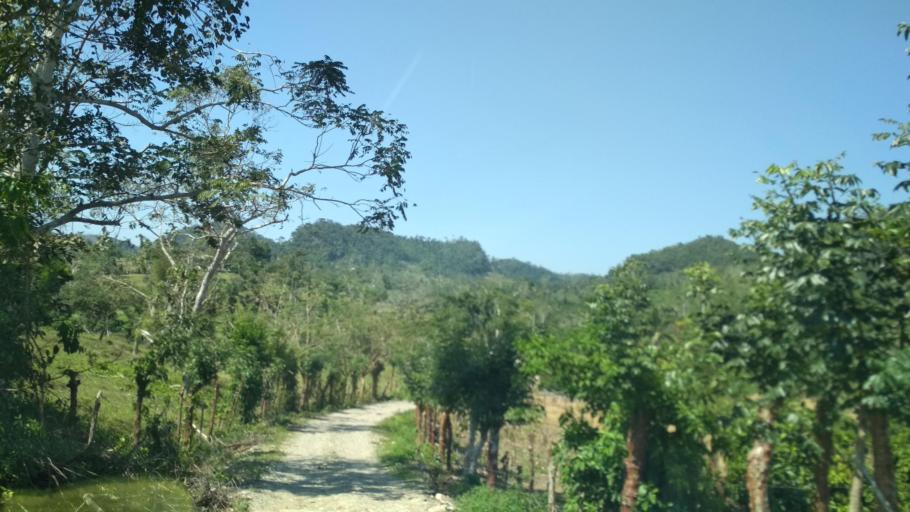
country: MX
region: Veracruz
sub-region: Papantla
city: Polutla
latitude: 20.4797
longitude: -97.2219
